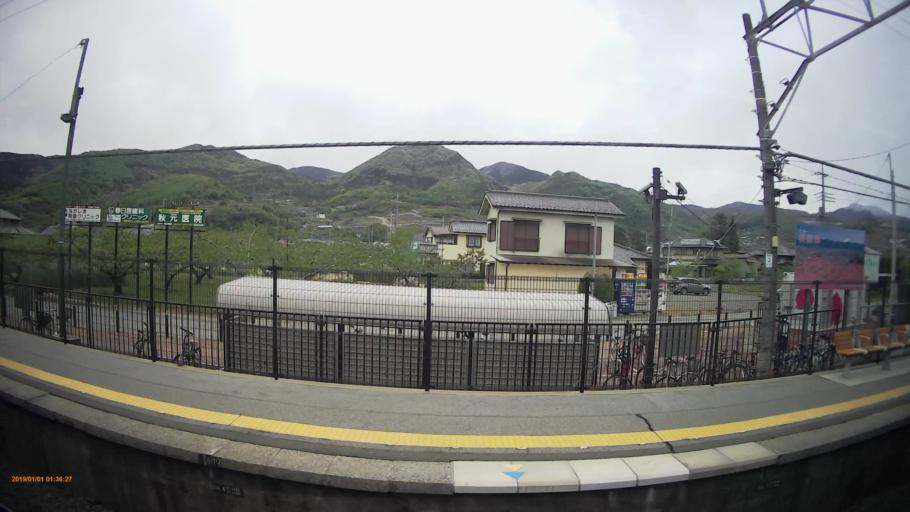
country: JP
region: Yamanashi
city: Isawa
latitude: 35.6738
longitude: 138.6593
